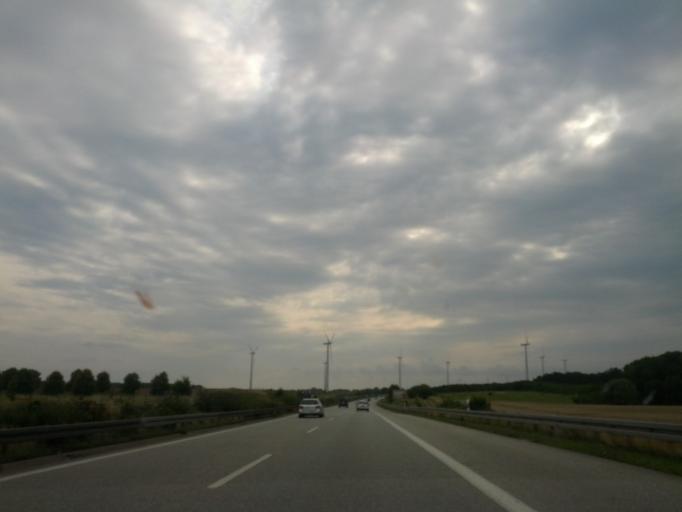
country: DE
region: Mecklenburg-Vorpommern
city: Jurgenshagen
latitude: 53.9770
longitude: 11.9140
